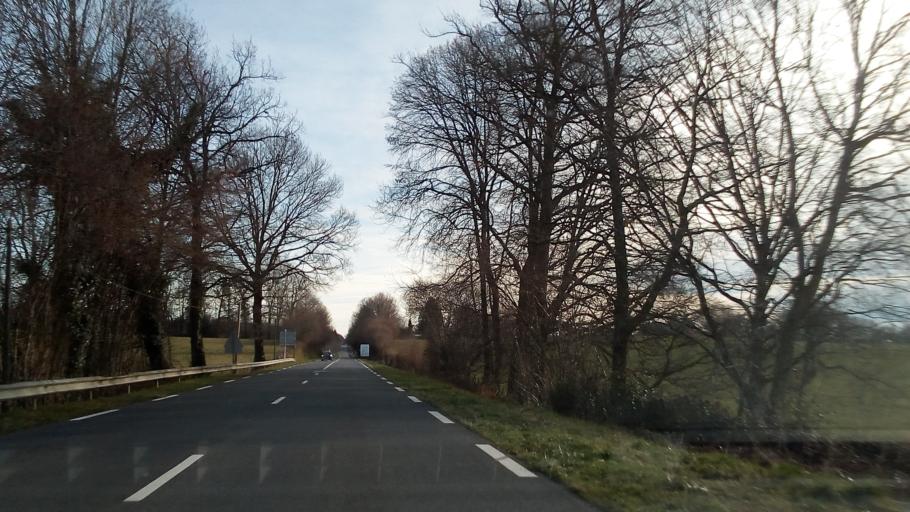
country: FR
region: Limousin
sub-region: Departement de la Correze
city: Saint-Clement
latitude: 45.3851
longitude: 1.6376
